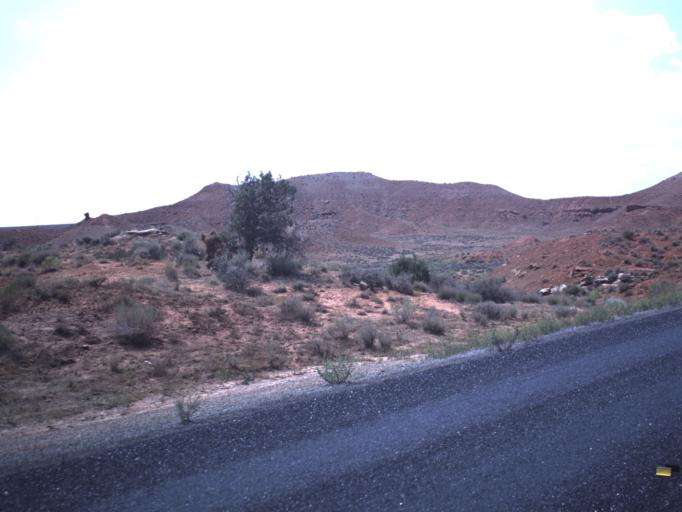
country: US
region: Utah
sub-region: Uintah County
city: Maeser
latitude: 40.4139
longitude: -109.7423
